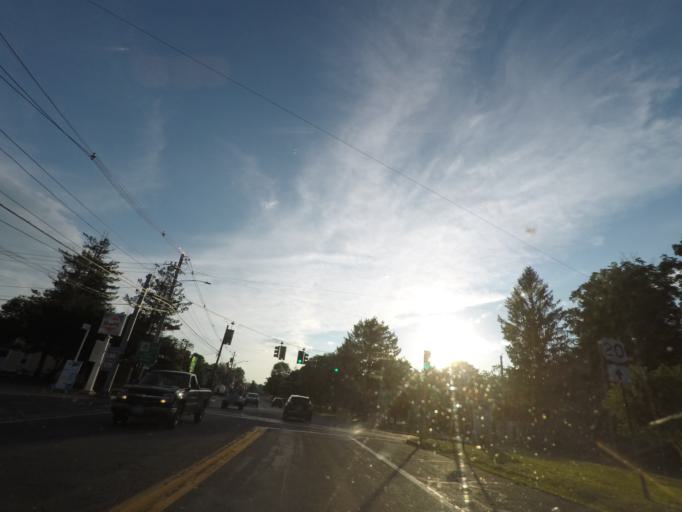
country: US
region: Massachusetts
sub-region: Hampden County
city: Brimfield
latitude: 42.1224
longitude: -72.2002
